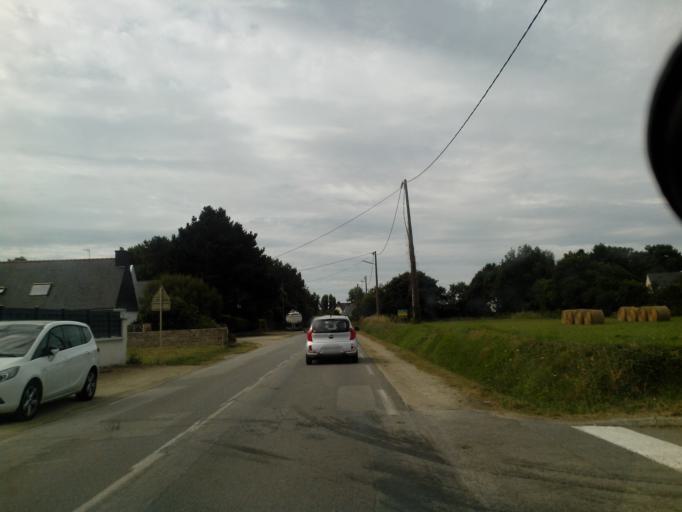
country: FR
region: Brittany
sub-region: Departement du Morbihan
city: Erdeven
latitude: 47.6376
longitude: -3.1561
